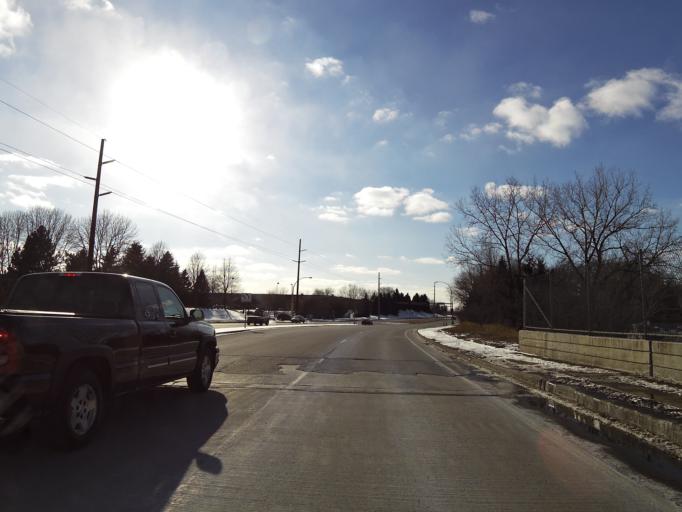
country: US
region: Minnesota
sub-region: Dakota County
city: Burnsville
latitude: 44.7524
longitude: -93.2864
